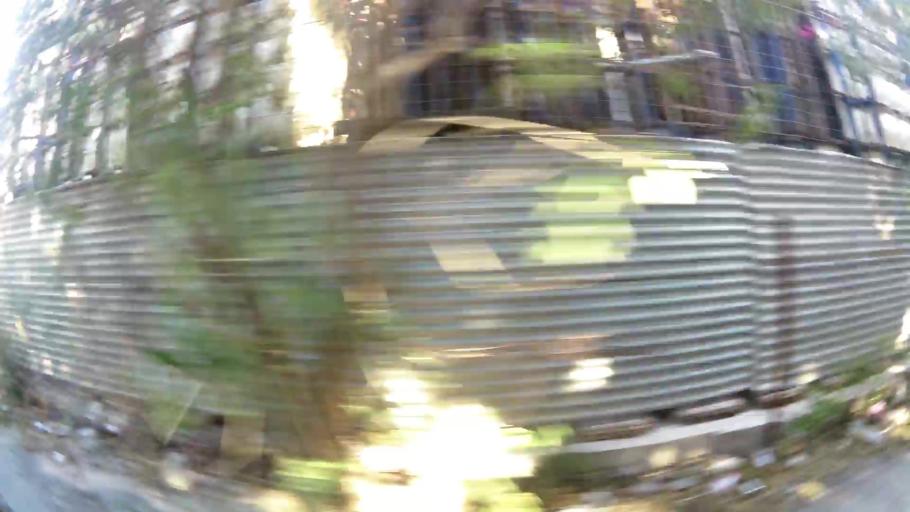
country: GR
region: Attica
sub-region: Nomarchia Athinas
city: Lykovrysi
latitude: 38.0869
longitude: 23.7816
